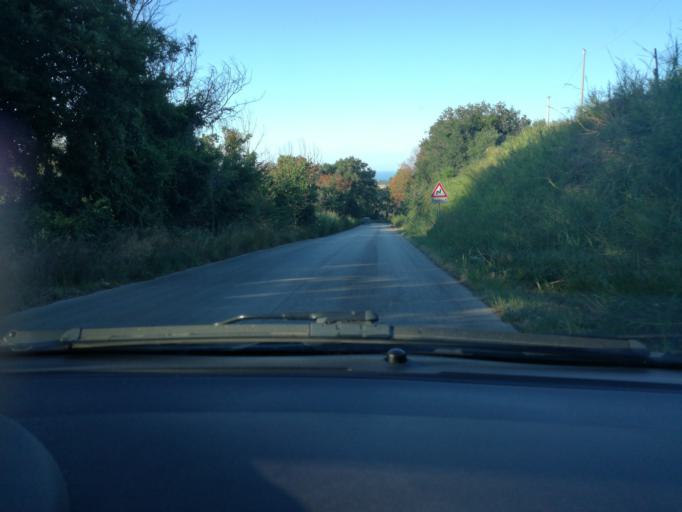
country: IT
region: Molise
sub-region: Provincia di Campobasso
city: Guglionesi
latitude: 41.9281
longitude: 14.9260
